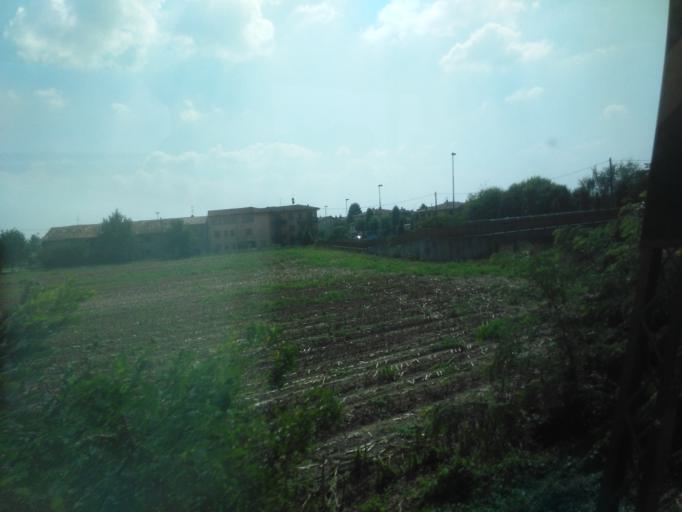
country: IT
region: Lombardy
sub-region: Provincia di Bergamo
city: Cortenuova
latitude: 45.5281
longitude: 9.8047
